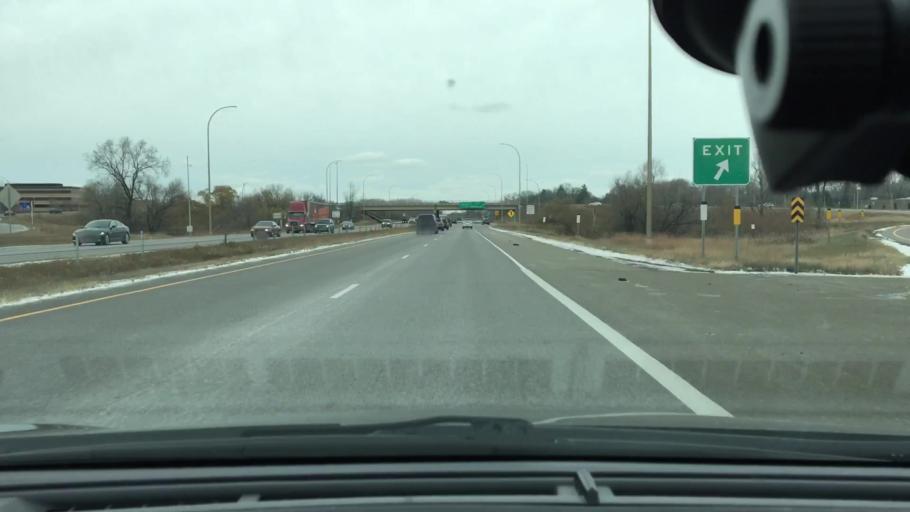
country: US
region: Minnesota
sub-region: Hennepin County
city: New Hope
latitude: 45.0551
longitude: -93.4008
